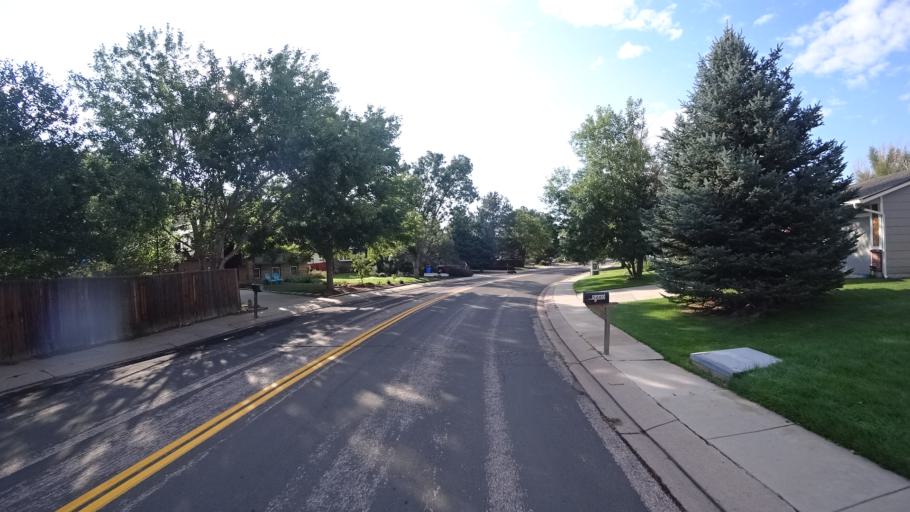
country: US
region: Colorado
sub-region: El Paso County
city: Manitou Springs
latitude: 38.9104
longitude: -104.8589
